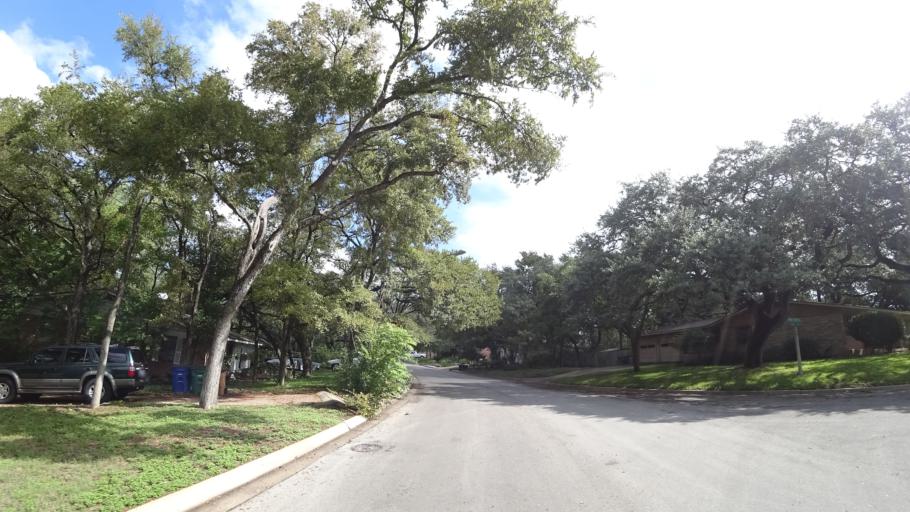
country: US
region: Texas
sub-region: Travis County
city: West Lake Hills
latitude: 30.3455
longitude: -97.7440
